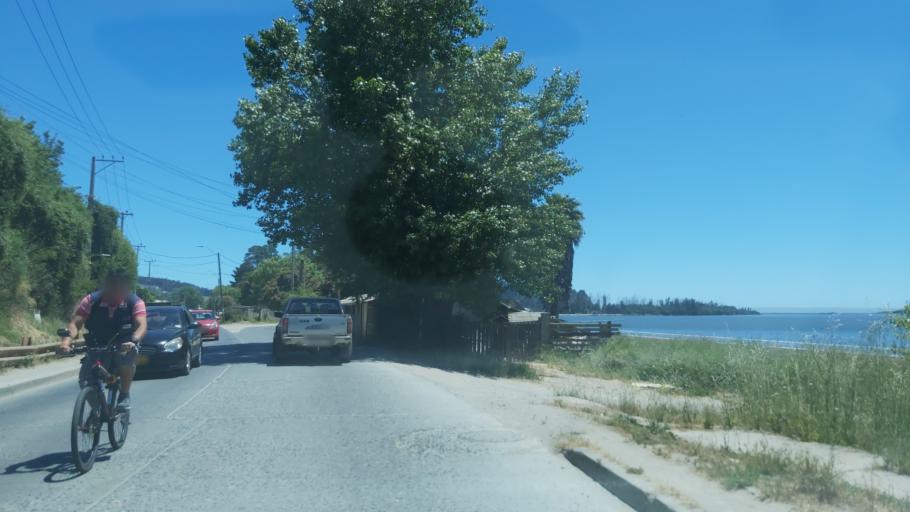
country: CL
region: Maule
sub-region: Provincia de Talca
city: Constitucion
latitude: -35.3403
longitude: -72.3967
